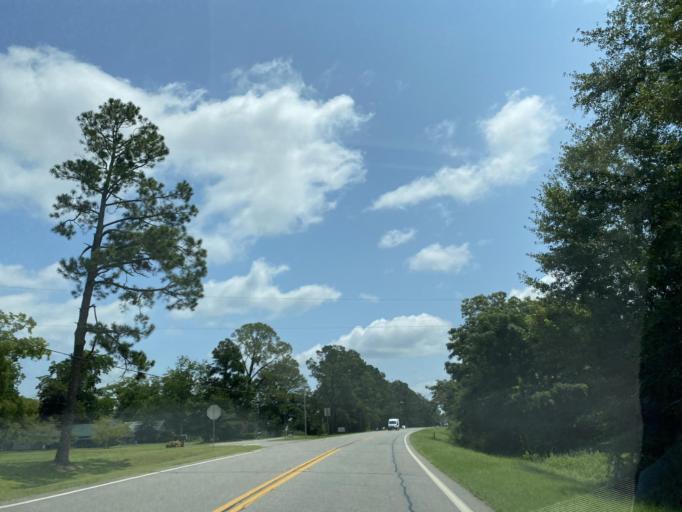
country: US
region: Georgia
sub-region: Telfair County
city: Helena
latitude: 32.0176
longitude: -83.0757
